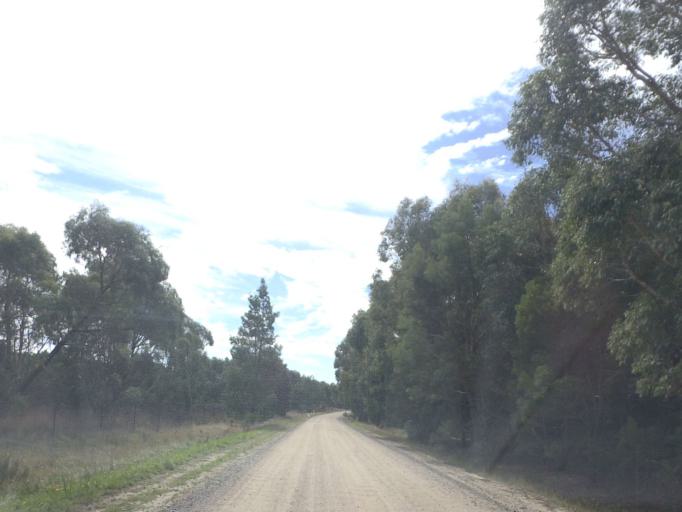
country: AU
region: Victoria
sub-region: Hume
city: Sunbury
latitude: -37.3742
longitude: 144.5493
